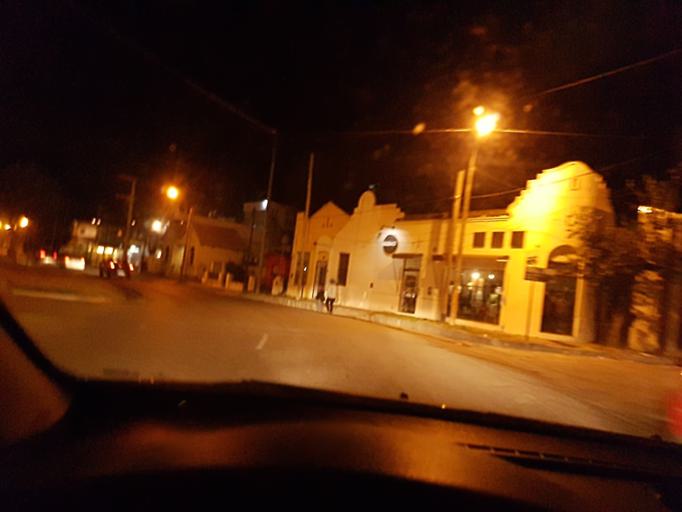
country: AR
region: Cordoba
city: Villa Allende
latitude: -31.2913
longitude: -64.2919
